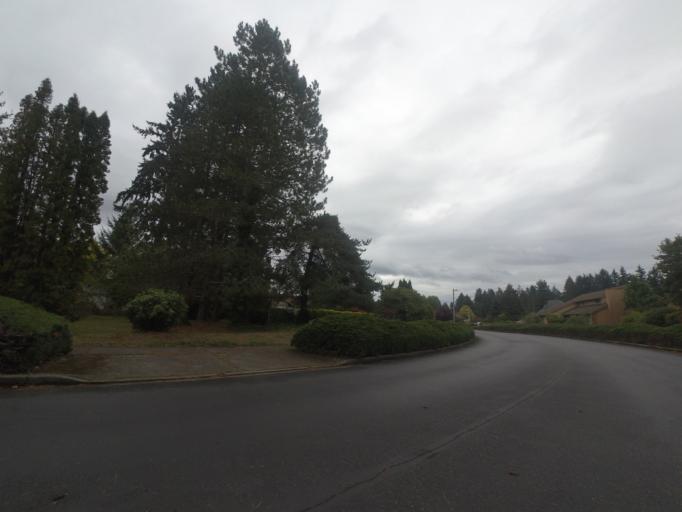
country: US
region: Washington
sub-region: Pierce County
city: Lakewood
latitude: 47.1552
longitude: -122.5176
